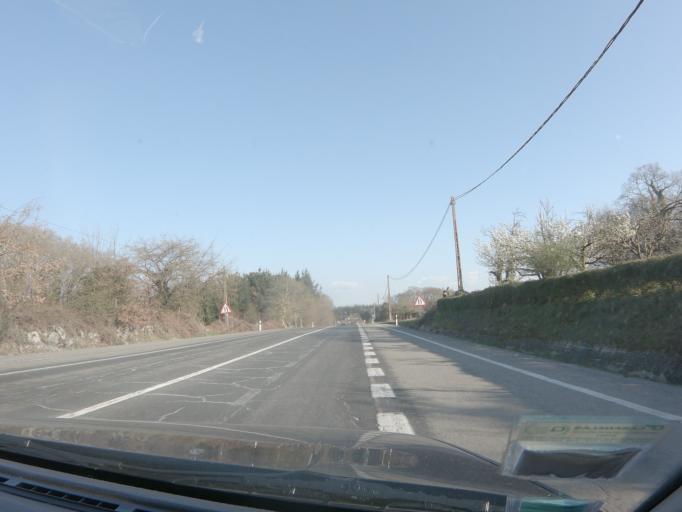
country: ES
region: Galicia
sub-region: Provincia de Lugo
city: Corgo
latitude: 42.9543
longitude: -7.4642
